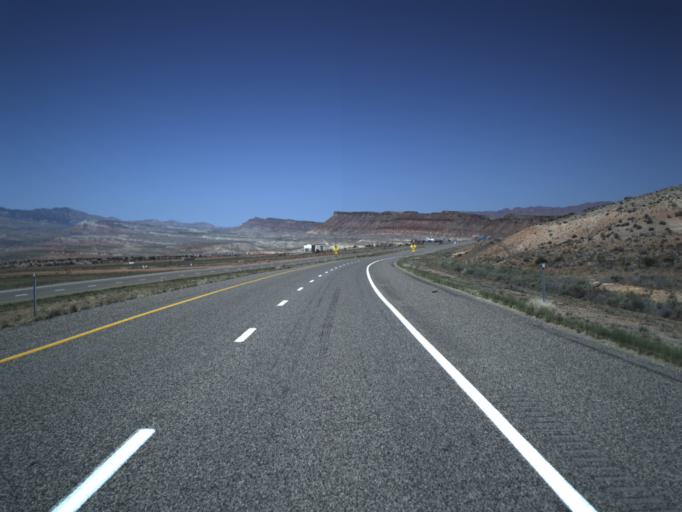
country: US
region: Utah
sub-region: Washington County
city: Saint George
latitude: 37.0182
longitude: -113.5968
